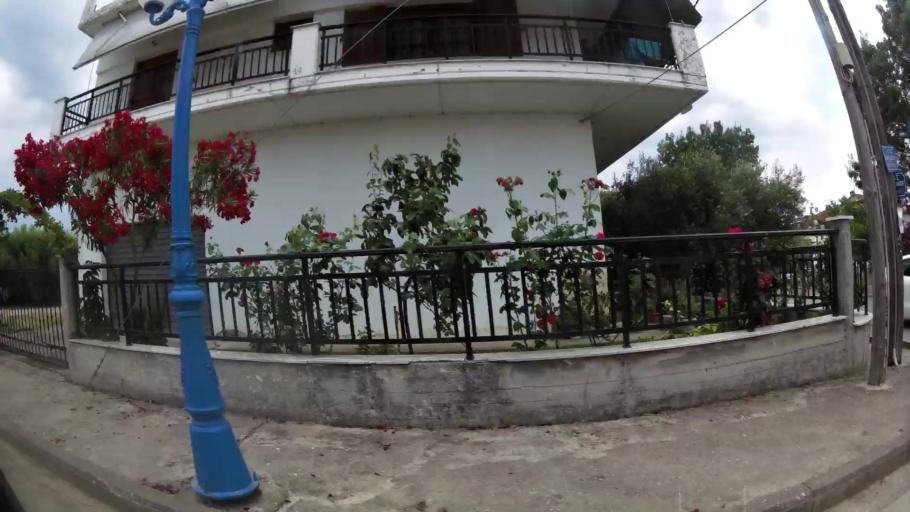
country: GR
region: Central Macedonia
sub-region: Nomos Pierias
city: Kallithea
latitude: 40.2780
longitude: 22.5772
